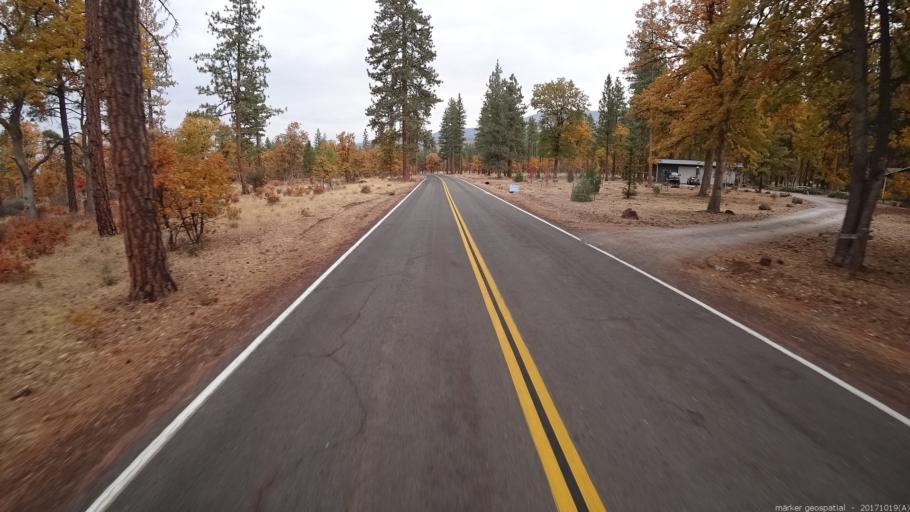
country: US
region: California
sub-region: Shasta County
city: Burney
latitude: 41.1189
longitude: -121.3316
